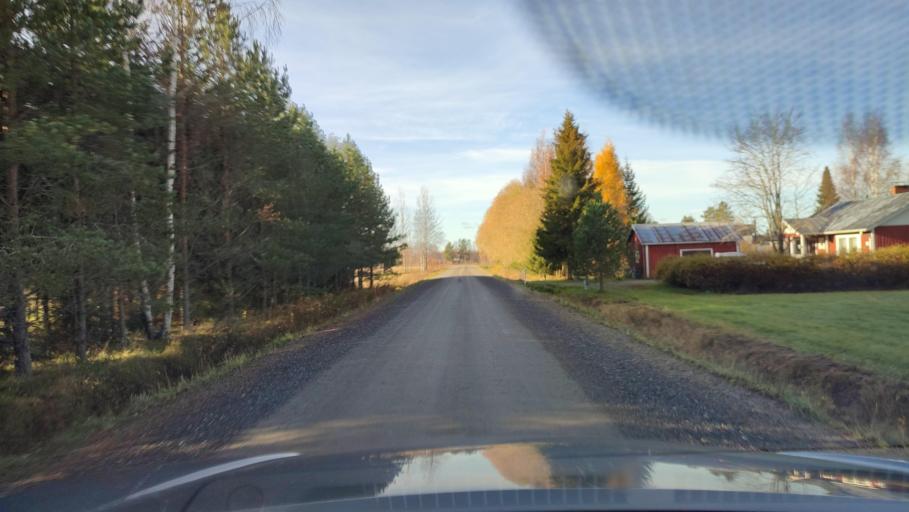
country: FI
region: Southern Ostrobothnia
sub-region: Suupohja
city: Teuva
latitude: 62.4563
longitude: 21.6303
